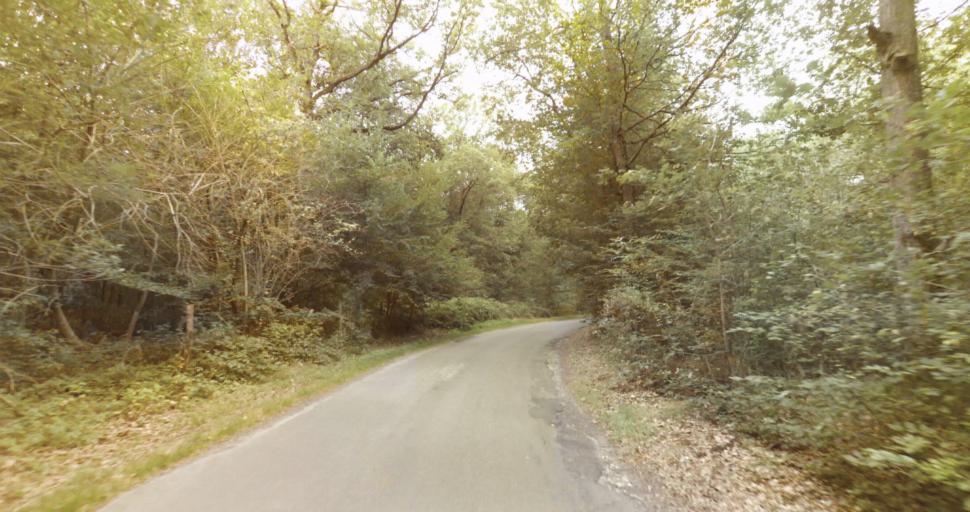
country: FR
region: Haute-Normandie
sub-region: Departement de l'Eure
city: La Couture-Boussey
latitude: 48.9016
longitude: 1.3640
